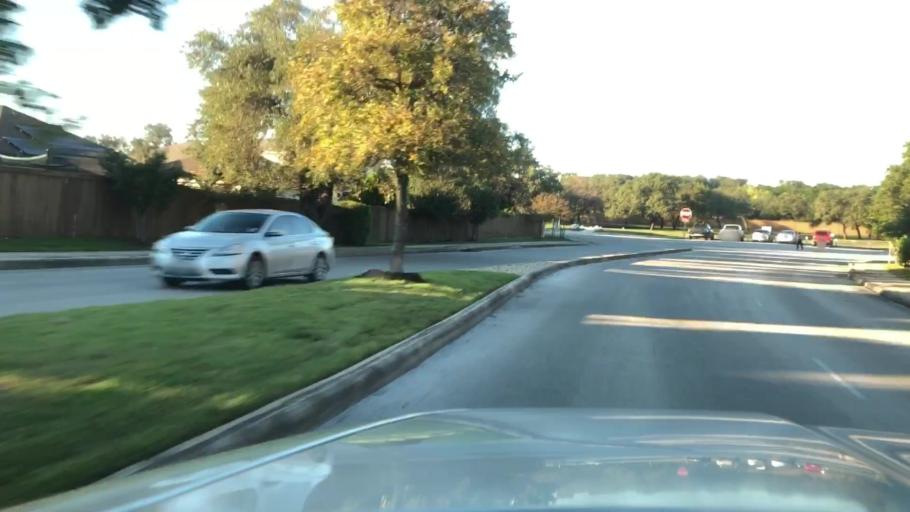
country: US
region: Texas
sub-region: Bexar County
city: Helotes
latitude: 29.5508
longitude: -98.6464
